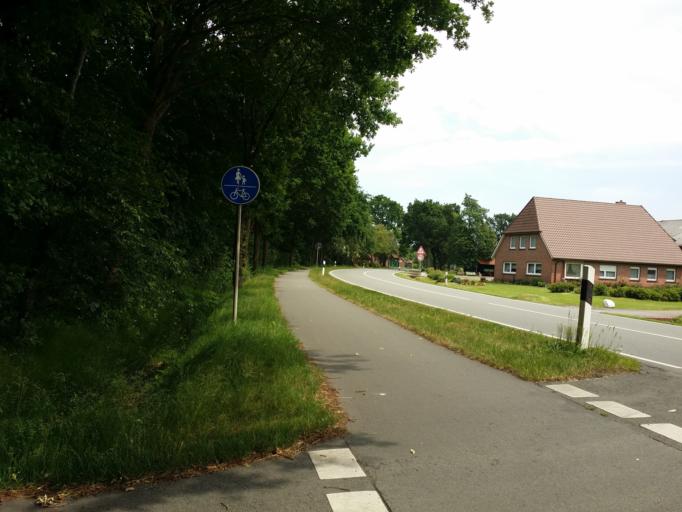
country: DE
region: Lower Saxony
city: Wiefelstede
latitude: 53.2458
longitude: 8.1384
